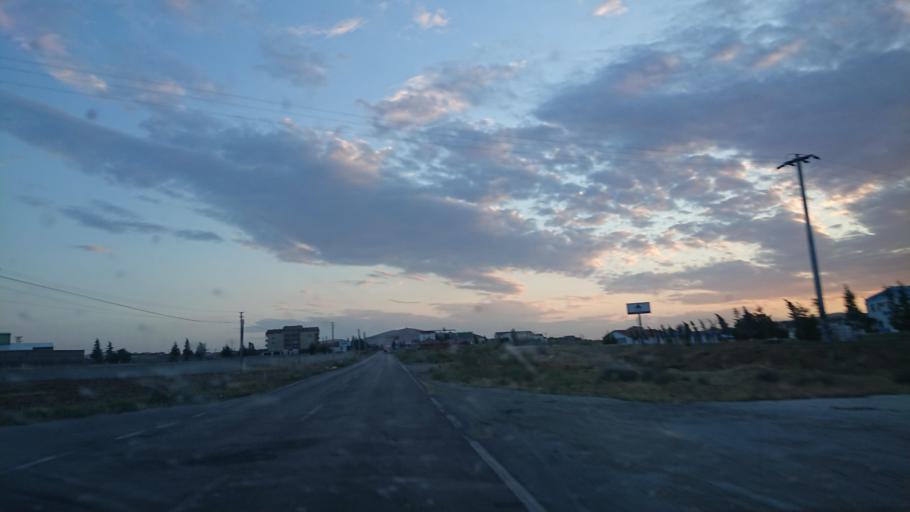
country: TR
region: Aksaray
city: Balci
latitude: 38.7573
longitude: 34.0783
